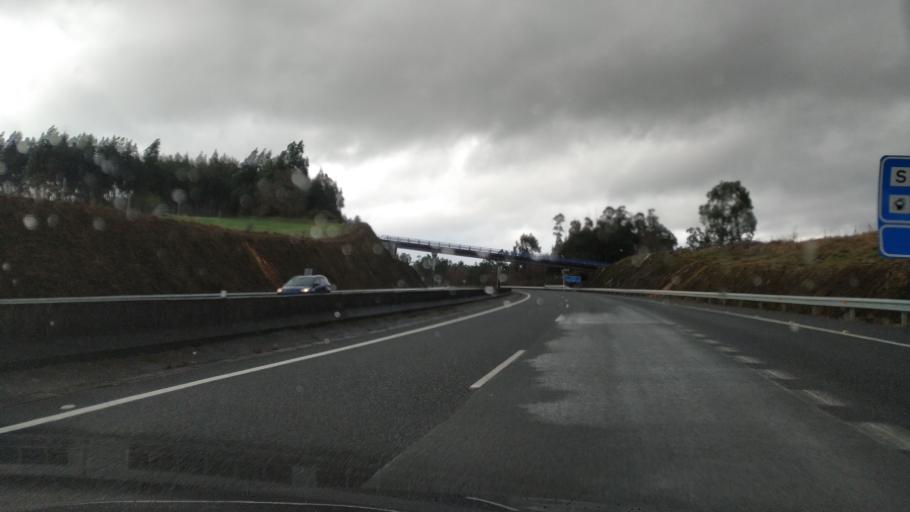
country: ES
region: Galicia
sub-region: Provincia de Pontevedra
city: Silleda
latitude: 42.7151
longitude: -8.2391
